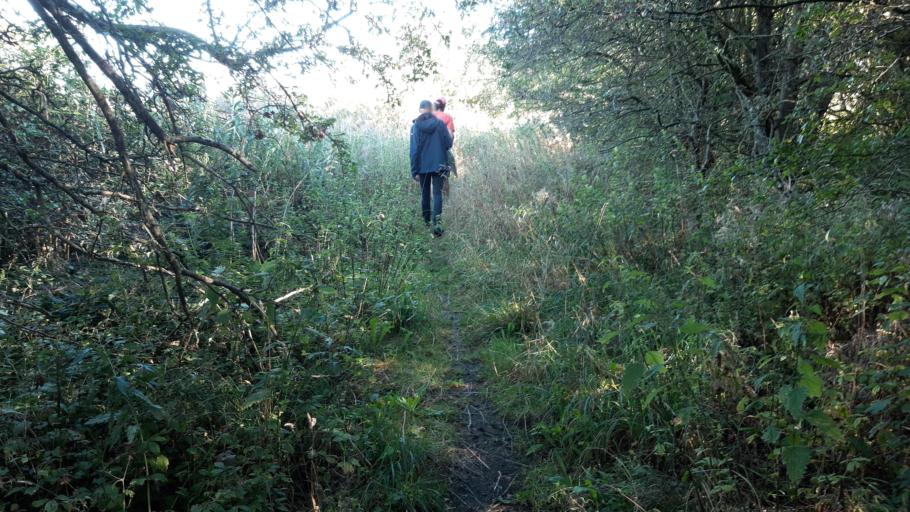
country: DK
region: Capital Region
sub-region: Ballerup Kommune
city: Ballerup
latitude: 55.7251
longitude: 12.3336
